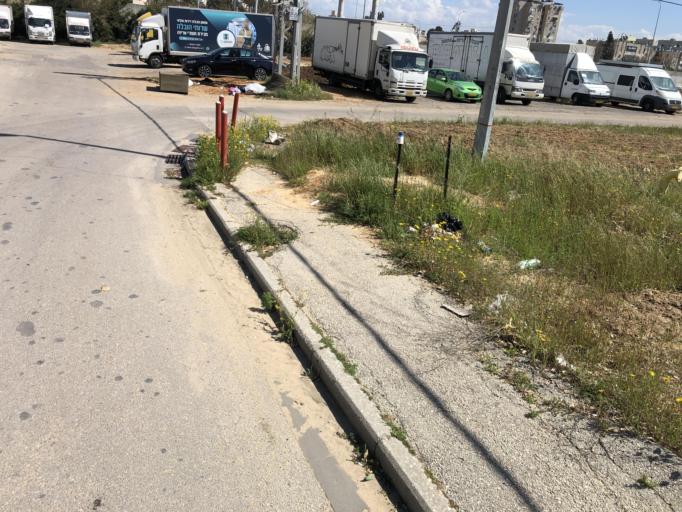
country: IL
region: Tel Aviv
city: Bat Yam
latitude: 32.0063
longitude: 34.7597
